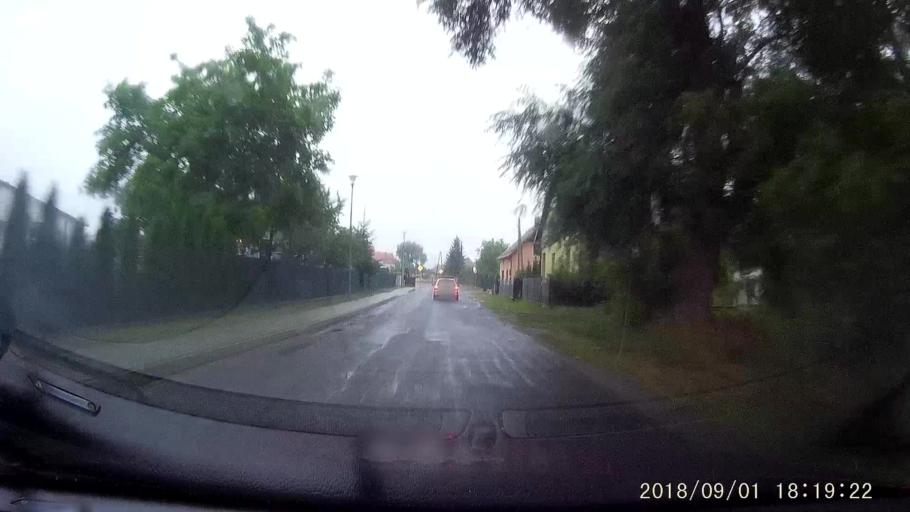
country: PL
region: Lower Silesian Voivodeship
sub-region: Powiat zgorzelecki
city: Piensk
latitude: 51.2550
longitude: 15.0458
